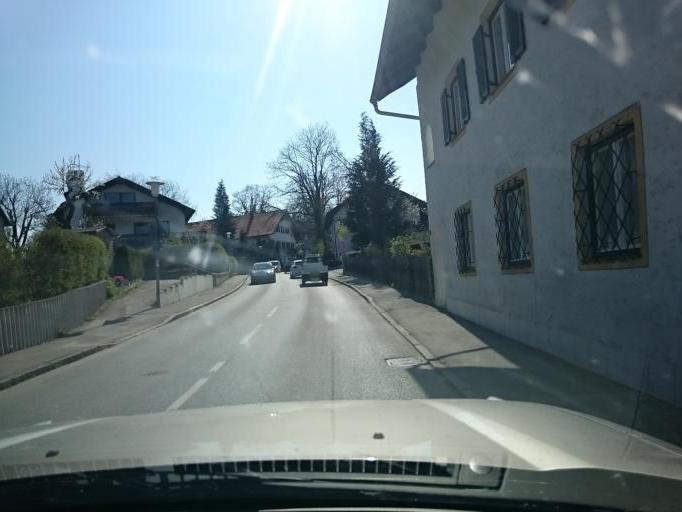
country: DE
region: Bavaria
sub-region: Upper Bavaria
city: Murnau am Staffelsee
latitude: 47.6773
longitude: 11.2044
